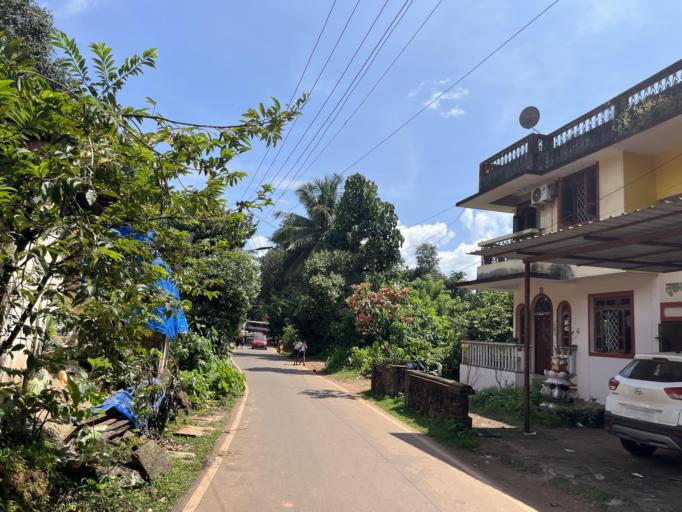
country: IN
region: Goa
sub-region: North Goa
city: Ponda
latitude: 15.4007
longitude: 74.0124
